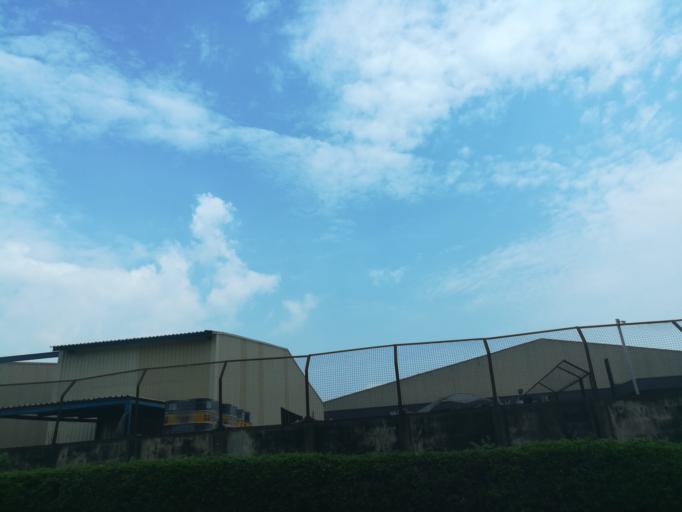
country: NG
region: Lagos
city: Ojota
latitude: 6.6059
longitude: 3.3677
